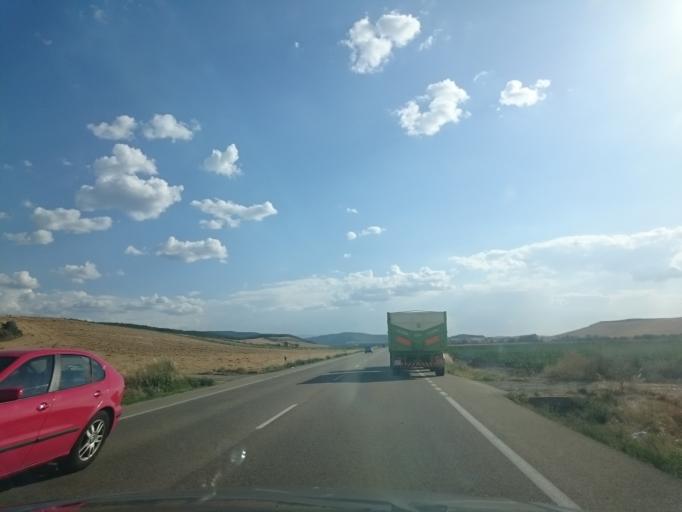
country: ES
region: La Rioja
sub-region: Provincia de La Rioja
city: Villarta-Quintana
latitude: 42.4469
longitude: -3.0497
